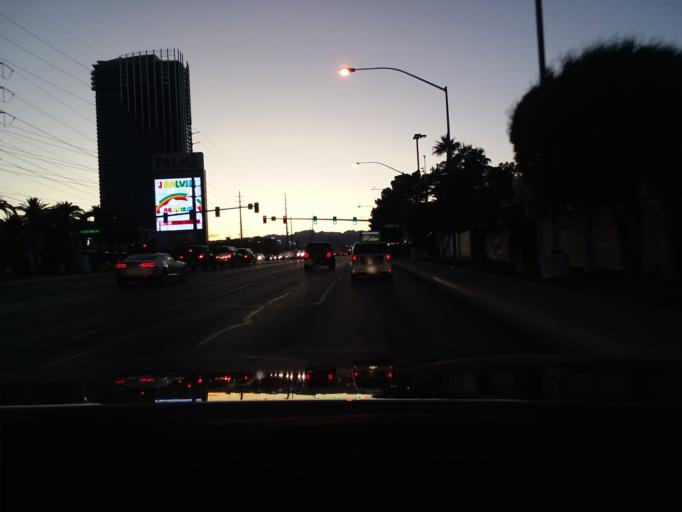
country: US
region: Nevada
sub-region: Clark County
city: Paradise
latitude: 36.1156
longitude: -115.1938
